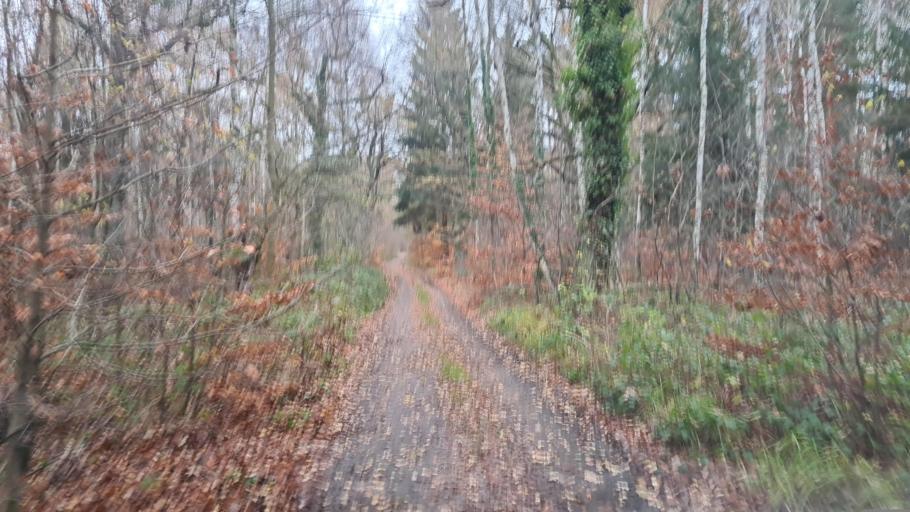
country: DE
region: Brandenburg
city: Crinitz
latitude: 51.7509
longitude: 13.7902
